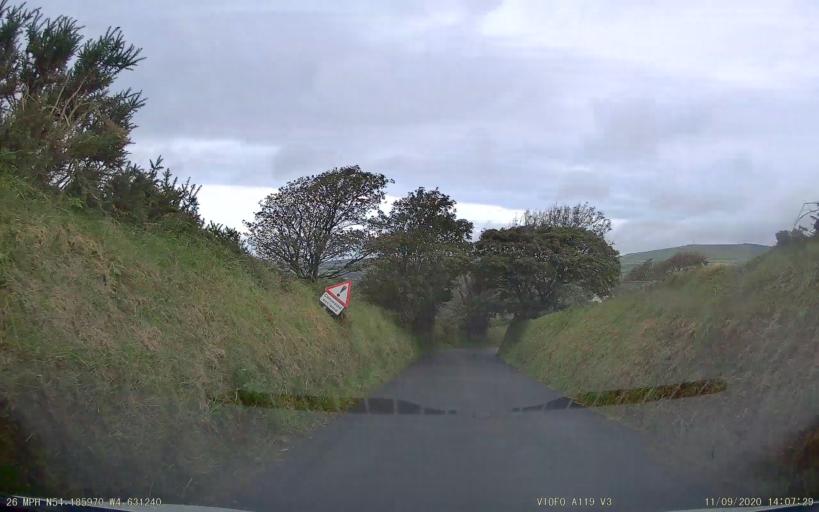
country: IM
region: Castletown
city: Castletown
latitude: 54.1860
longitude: -4.6312
